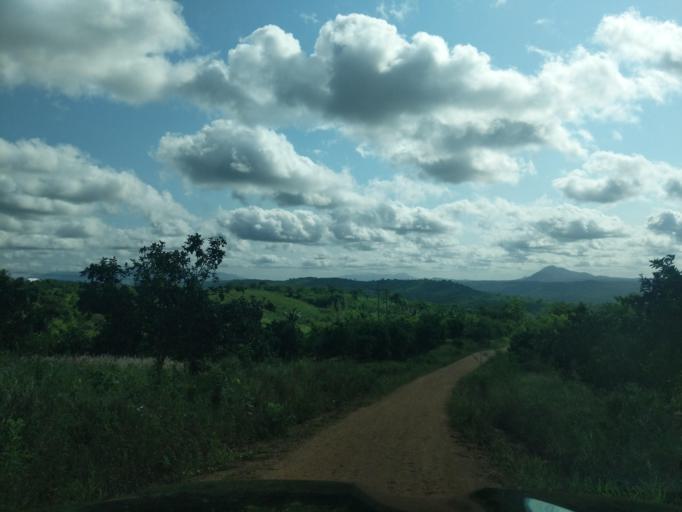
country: TZ
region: Tanga
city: Muheza
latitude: -5.4229
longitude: 38.6381
